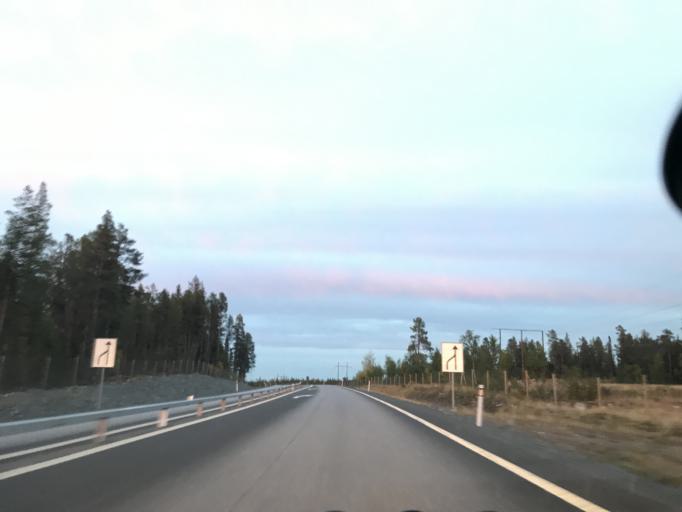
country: SE
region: Norrbotten
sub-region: Gallivare Kommun
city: Malmberget
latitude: 67.6729
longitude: 20.9138
